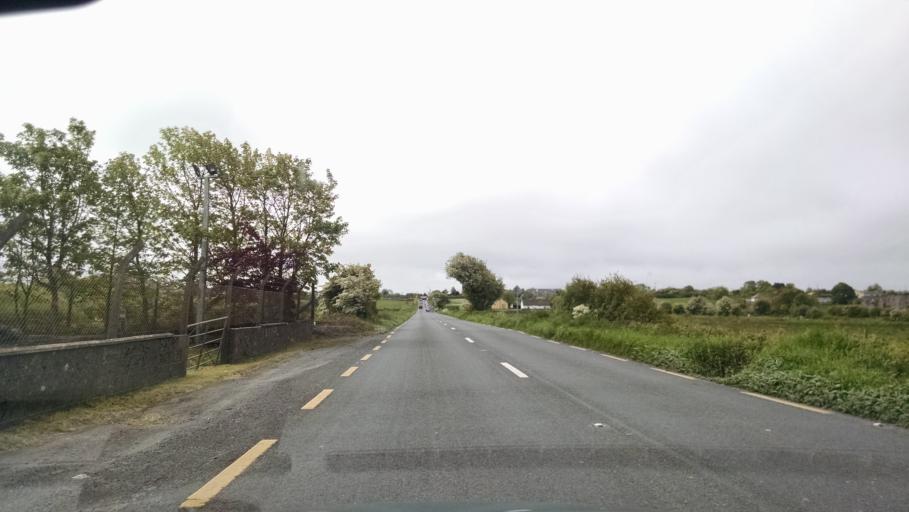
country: IE
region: Connaught
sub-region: County Galway
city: Gaillimh
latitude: 53.3199
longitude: -9.0218
